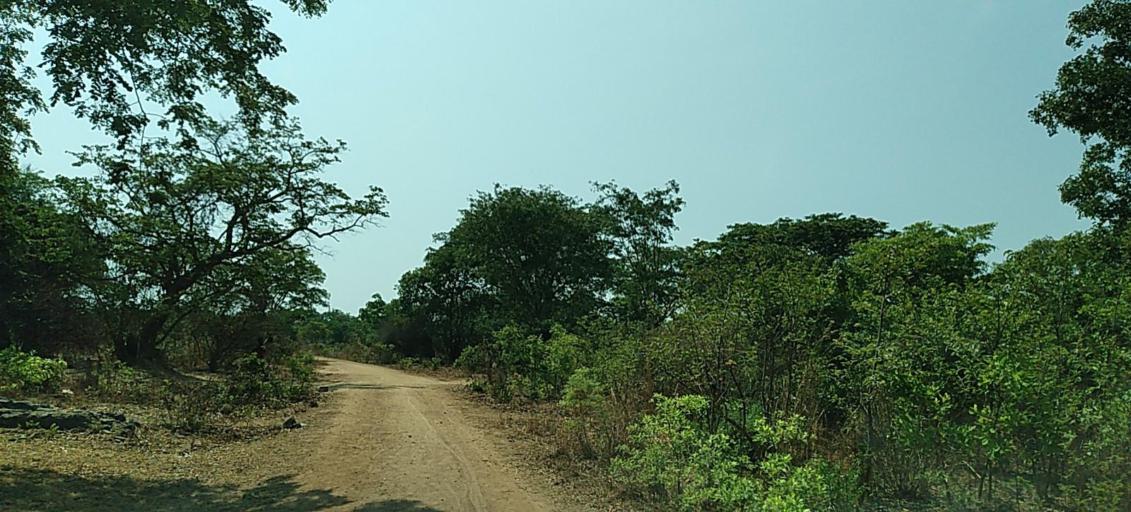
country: ZM
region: Copperbelt
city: Luanshya
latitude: -13.2814
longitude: 28.3172
